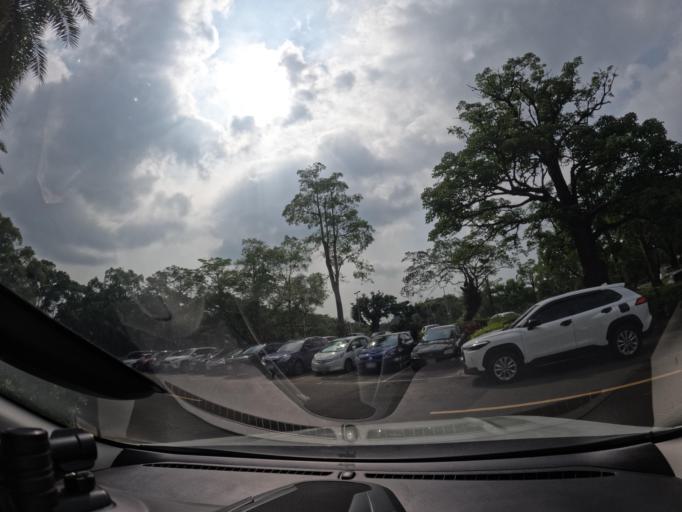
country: TW
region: Taiwan
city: Daxi
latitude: 24.8812
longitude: 121.3263
